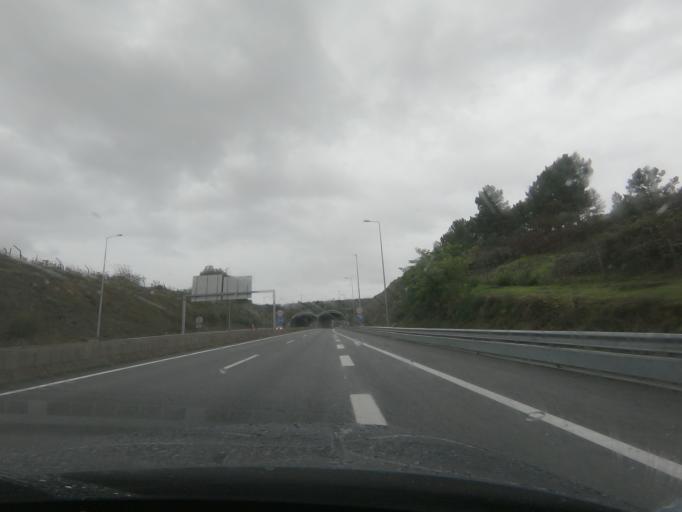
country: PT
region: Vila Real
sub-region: Vila Real
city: Vila Real
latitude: 41.2794
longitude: -7.7225
